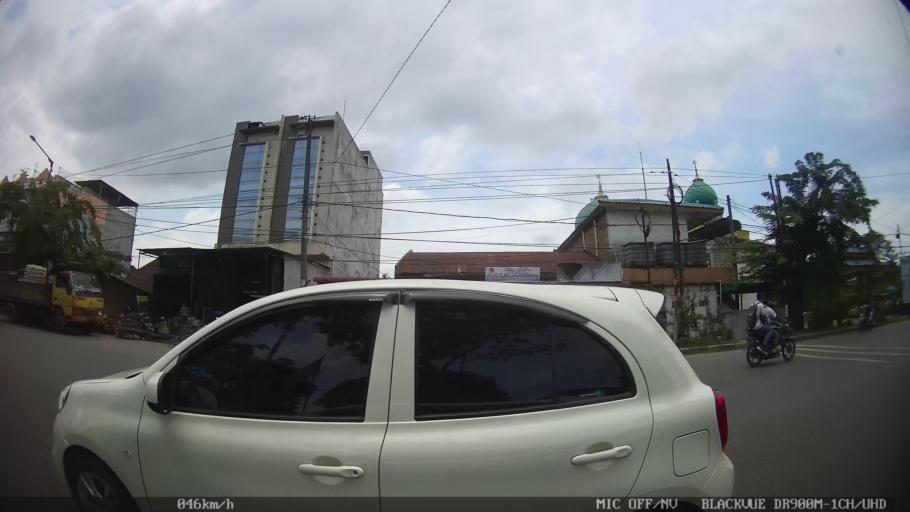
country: ID
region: North Sumatra
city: Labuhan Deli
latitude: 3.6893
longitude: 98.6684
